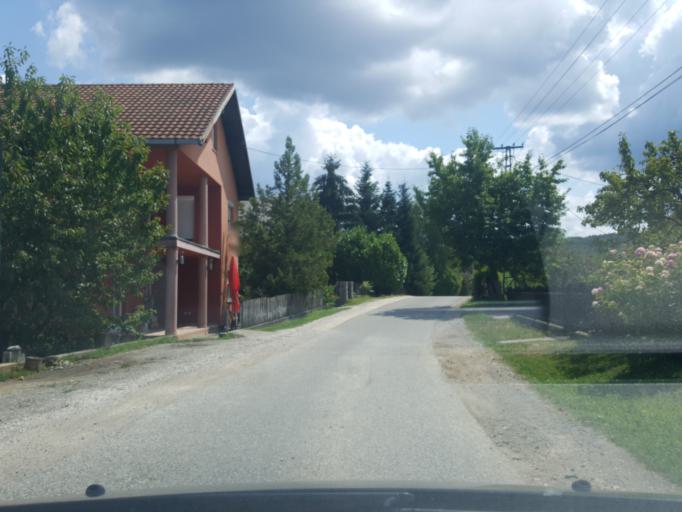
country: RS
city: Trsic
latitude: 44.5193
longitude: 19.2269
